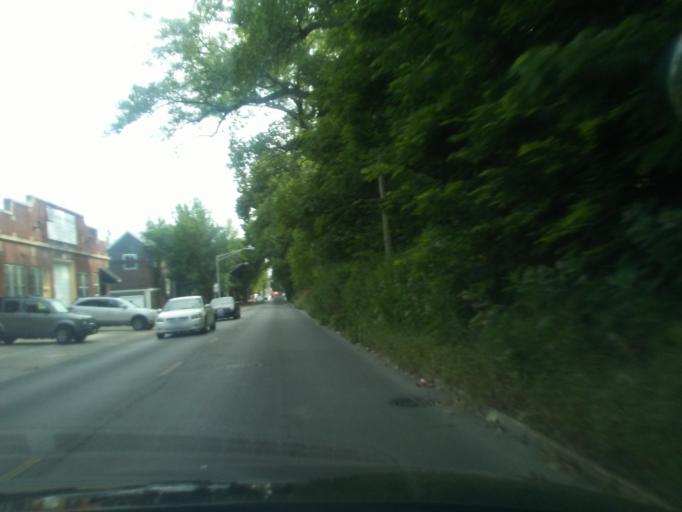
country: US
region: Illinois
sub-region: Cook County
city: Evanston
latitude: 41.9892
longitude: -87.6747
